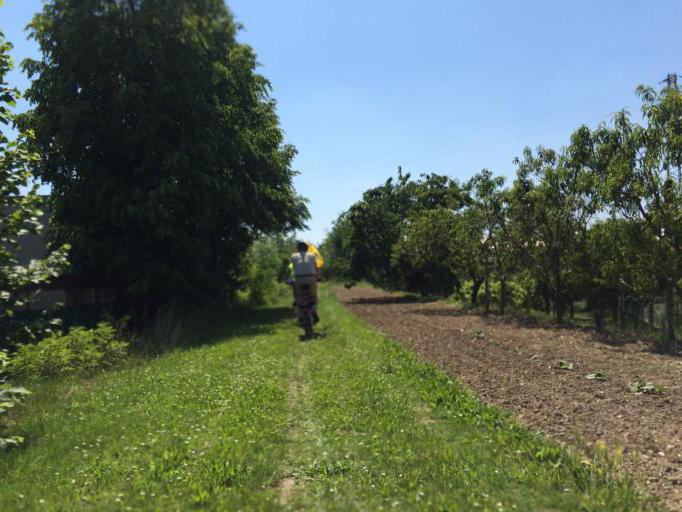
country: IT
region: Veneto
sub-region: Provincia di Vicenza
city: Sossano
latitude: 45.3528
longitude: 11.5057
